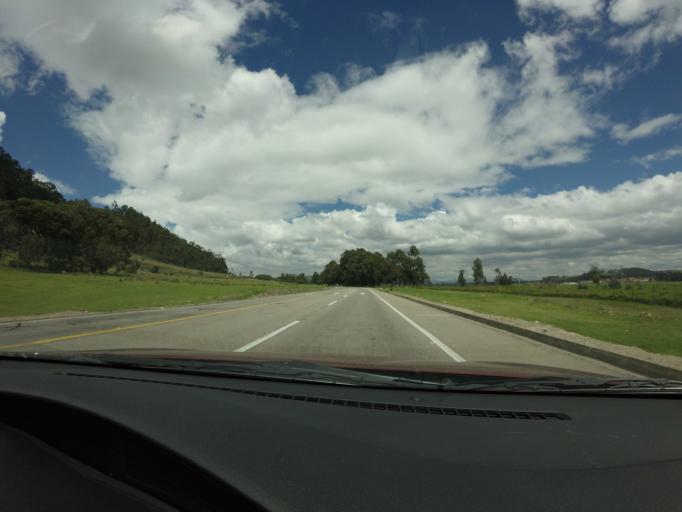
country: CO
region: Cundinamarca
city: Soacha
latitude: 4.5676
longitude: -74.2591
